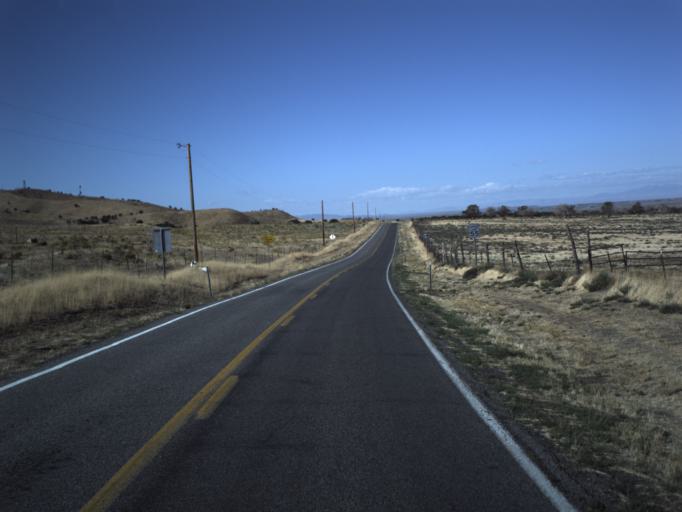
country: US
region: Utah
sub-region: Millard County
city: Delta
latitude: 39.3668
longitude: -112.3394
